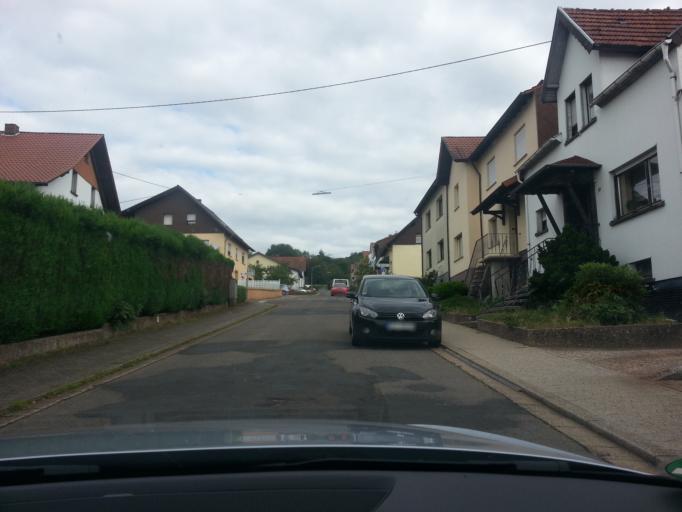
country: DE
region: Saarland
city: Eppelborn
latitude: 49.4615
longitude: 6.9622
